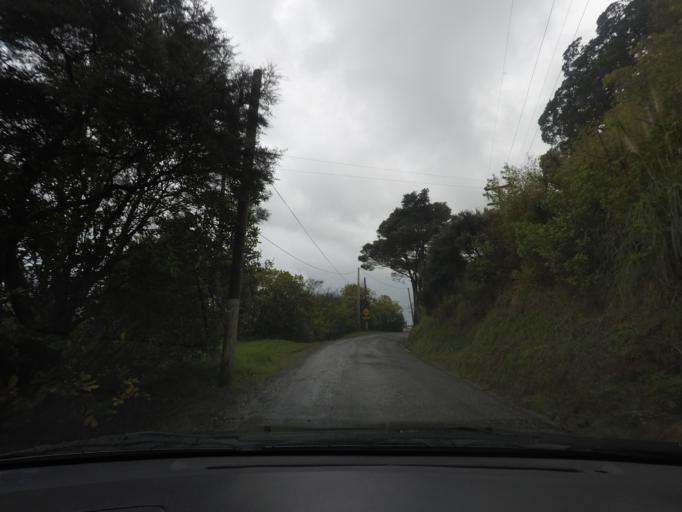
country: NZ
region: Auckland
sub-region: Auckland
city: Warkworth
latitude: -36.4833
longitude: 174.7278
